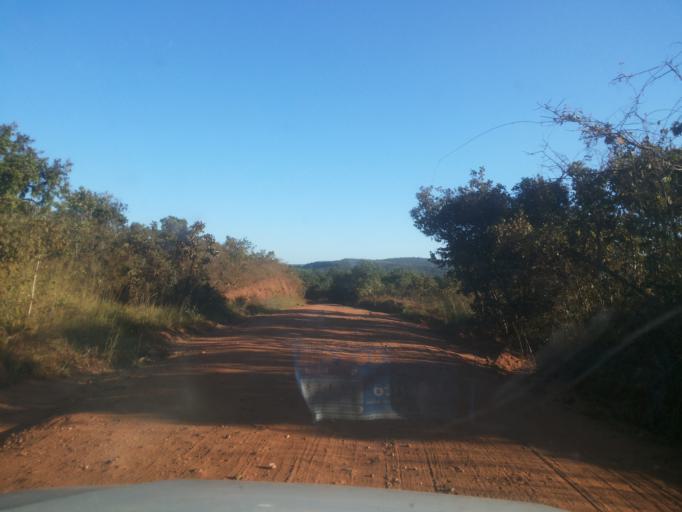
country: BR
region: Minas Gerais
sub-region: Campina Verde
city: Campina Verde
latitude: -19.3200
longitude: -49.8025
